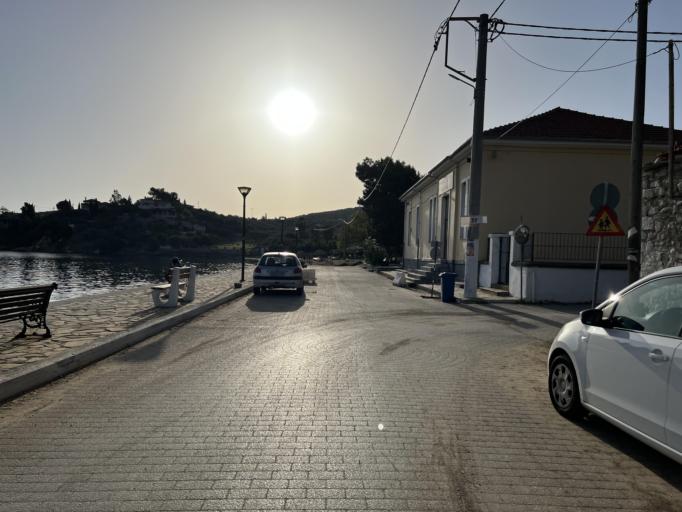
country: GR
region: Thessaly
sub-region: Nomos Magnisias
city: Sourpi
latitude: 39.1664
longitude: 22.8919
